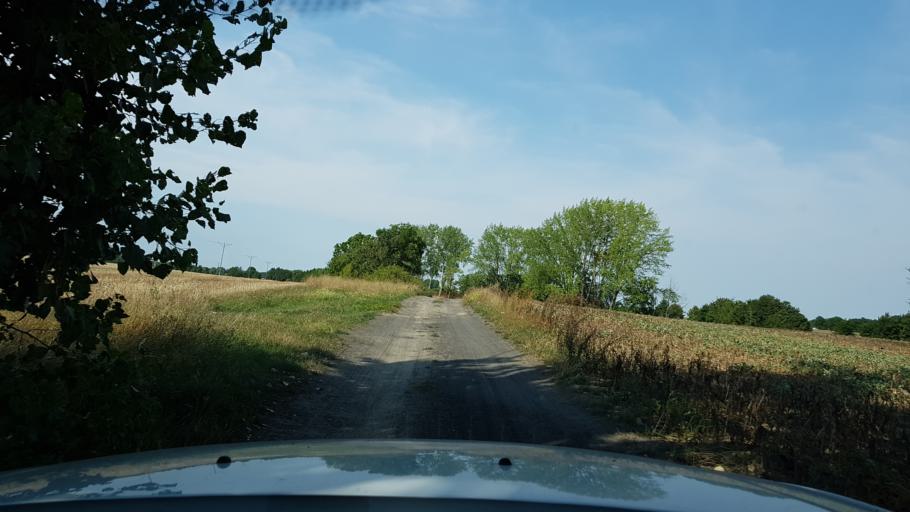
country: PL
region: West Pomeranian Voivodeship
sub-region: Powiat pyrzycki
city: Pyrzyce
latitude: 53.1173
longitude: 14.8855
